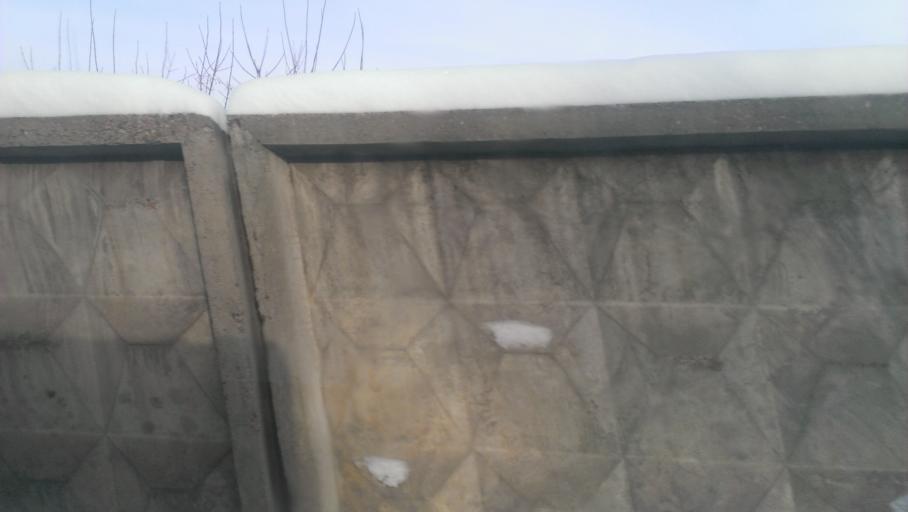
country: RU
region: Altai Krai
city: Nauchnyy Gorodok
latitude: 53.4220
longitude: 83.5200
